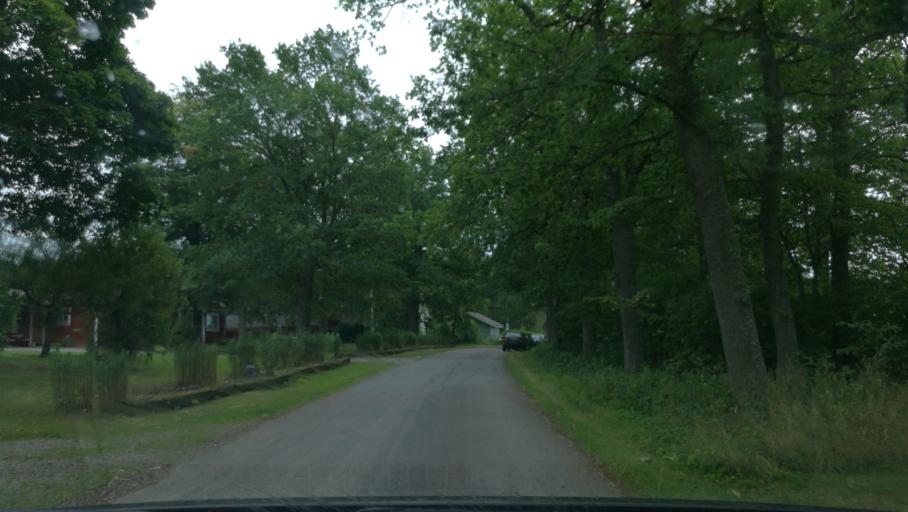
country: SE
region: Vaestmanland
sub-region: Vasteras
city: Tillberga
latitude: 59.7161
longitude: 16.6469
